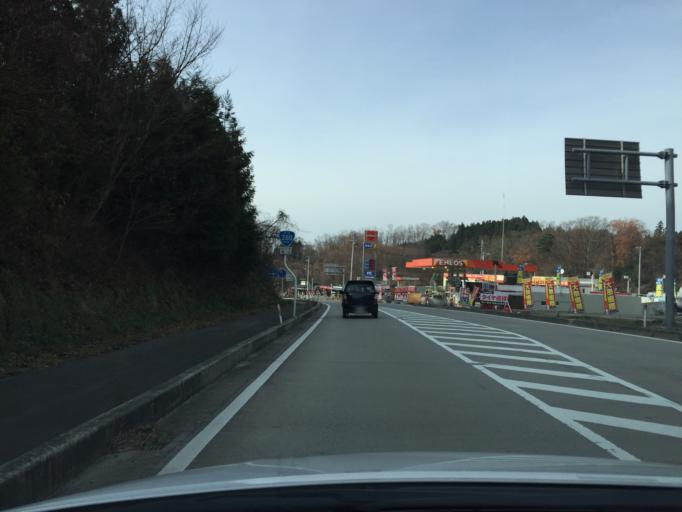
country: JP
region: Fukushima
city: Funehikimachi-funehiki
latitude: 37.4460
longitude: 140.5312
